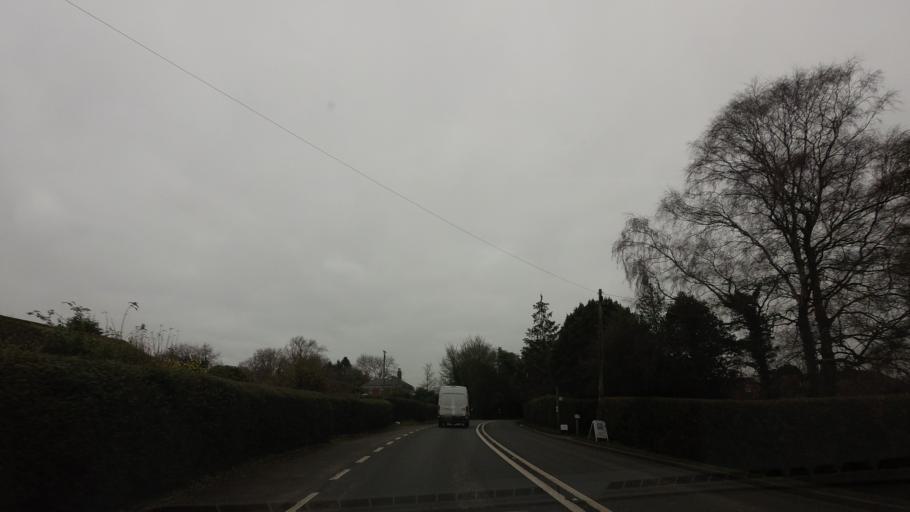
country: GB
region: England
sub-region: Kent
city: Cranbrook
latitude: 51.1194
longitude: 0.5558
